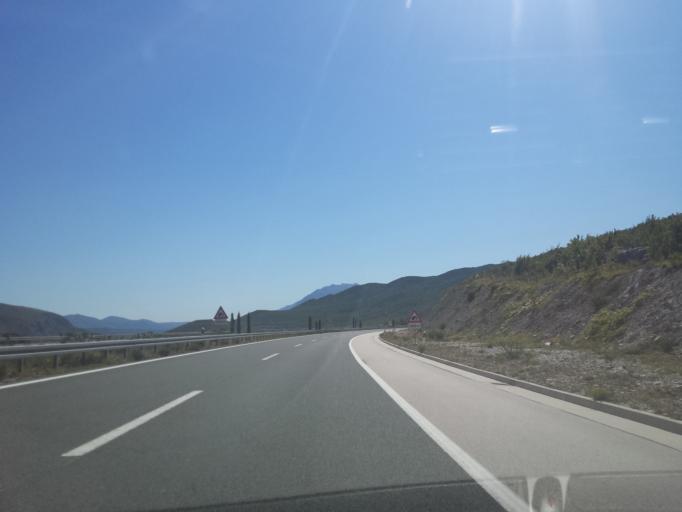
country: HR
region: Splitsko-Dalmatinska
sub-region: Grad Omis
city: Omis
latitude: 43.4910
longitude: 16.7963
